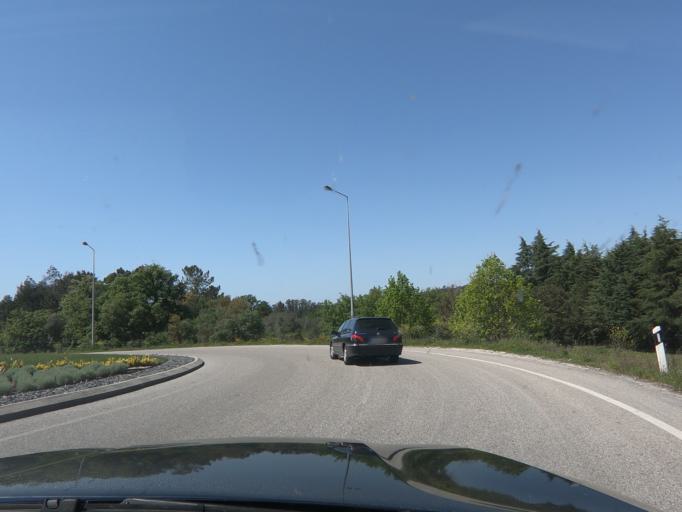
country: PT
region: Coimbra
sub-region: Lousa
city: Lousa
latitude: 40.1290
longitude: -8.2481
